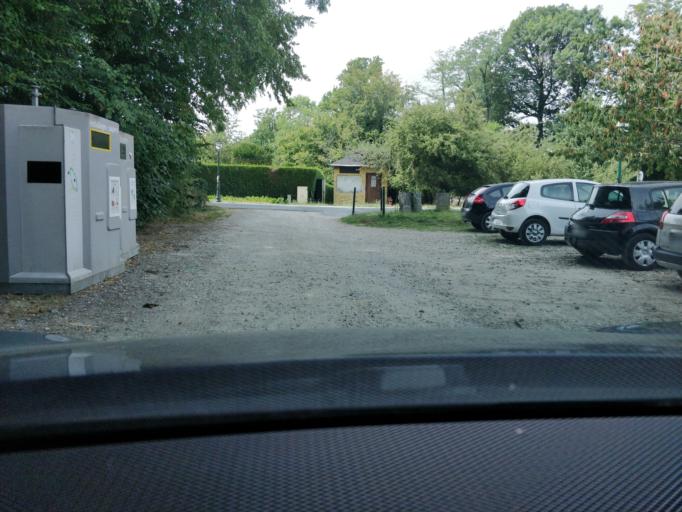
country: FR
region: Ile-de-France
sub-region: Departement de l'Essonne
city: Fontenay-les-Briis
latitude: 48.6461
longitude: 2.1530
